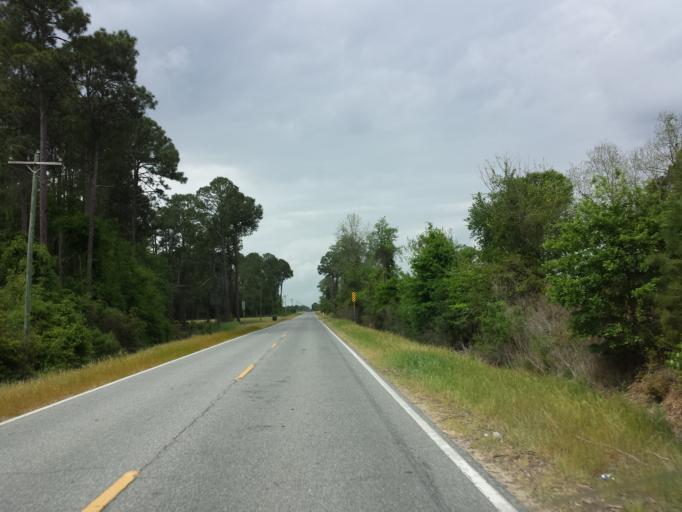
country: US
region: Georgia
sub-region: Tift County
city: Omega
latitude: 31.3030
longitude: -83.4723
